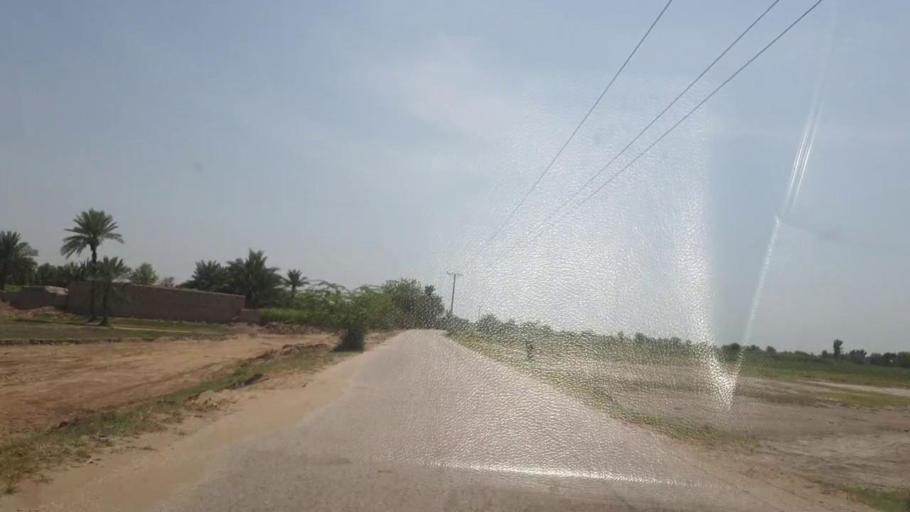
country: PK
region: Sindh
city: Bozdar
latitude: 27.0699
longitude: 68.5946
